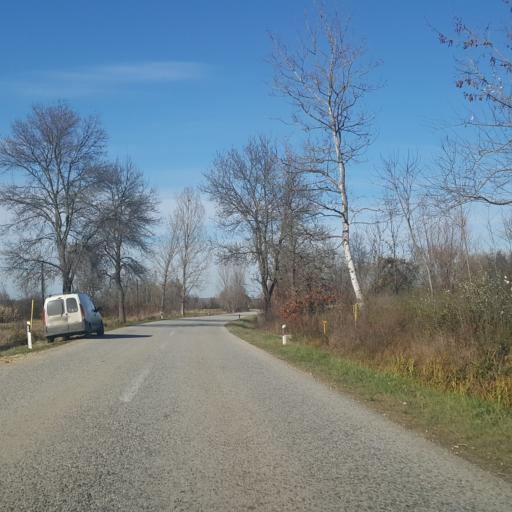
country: RS
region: Central Serbia
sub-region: Sumadijski Okrug
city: Topola
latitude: 44.2499
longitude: 20.8299
